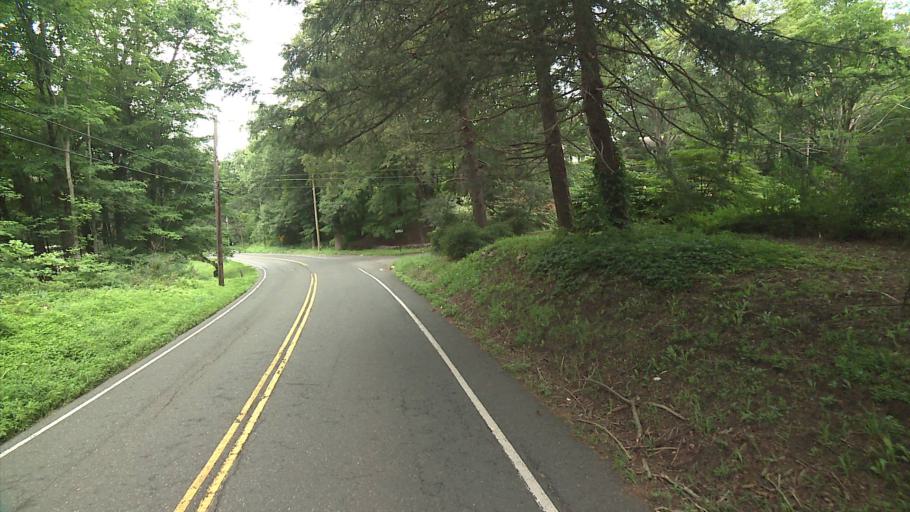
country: US
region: Connecticut
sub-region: Litchfield County
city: New Milford
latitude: 41.5677
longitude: -73.3218
